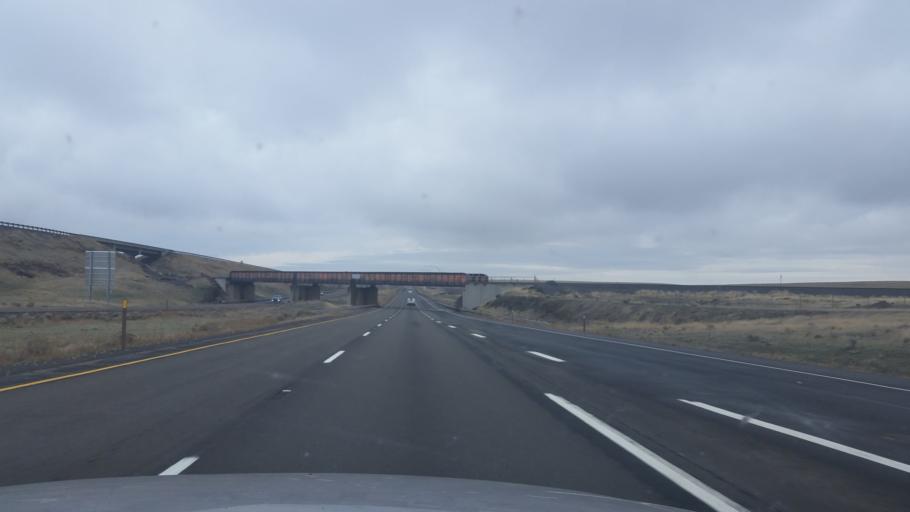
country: US
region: Washington
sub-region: Adams County
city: Ritzville
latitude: 47.1114
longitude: -118.3972
